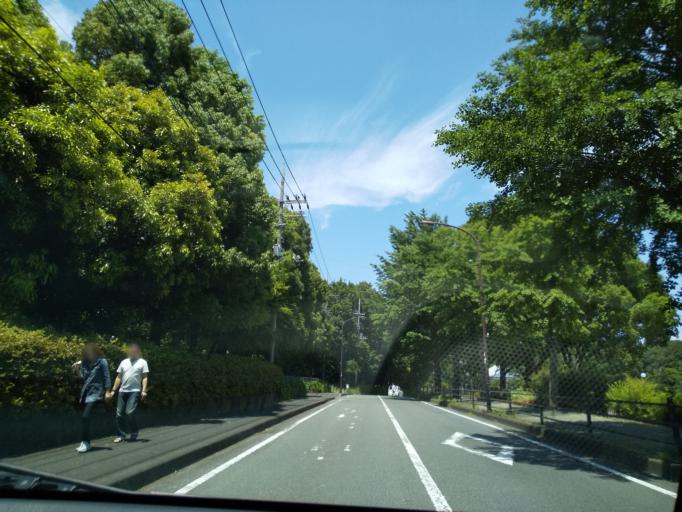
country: JP
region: Kanagawa
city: Zama
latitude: 35.5281
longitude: 139.3904
